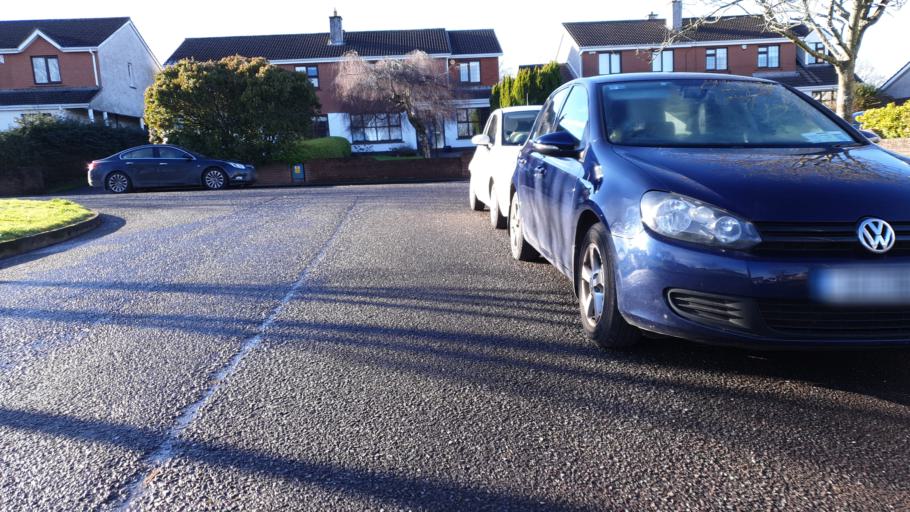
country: IE
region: Munster
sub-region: County Cork
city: Cork
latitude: 51.8929
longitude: -8.4239
